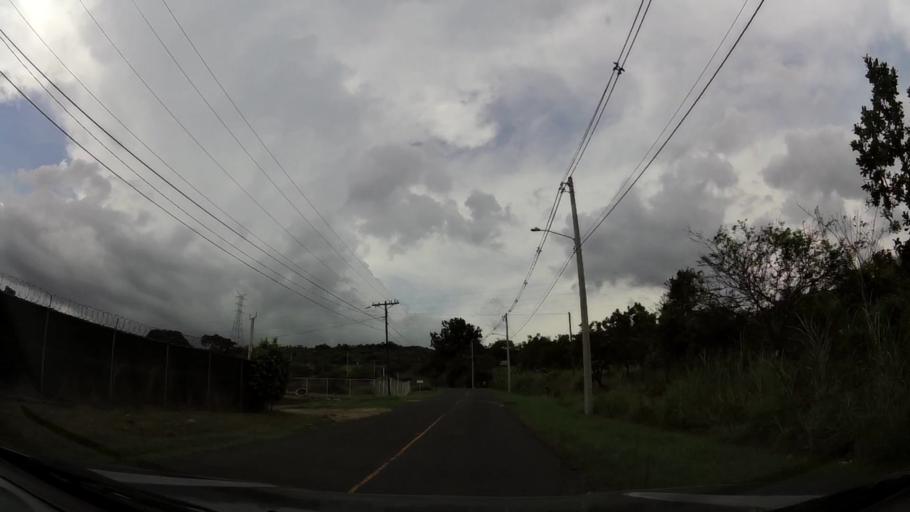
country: PA
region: Panama
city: Cabra Numero Uno
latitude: 9.1246
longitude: -79.3626
